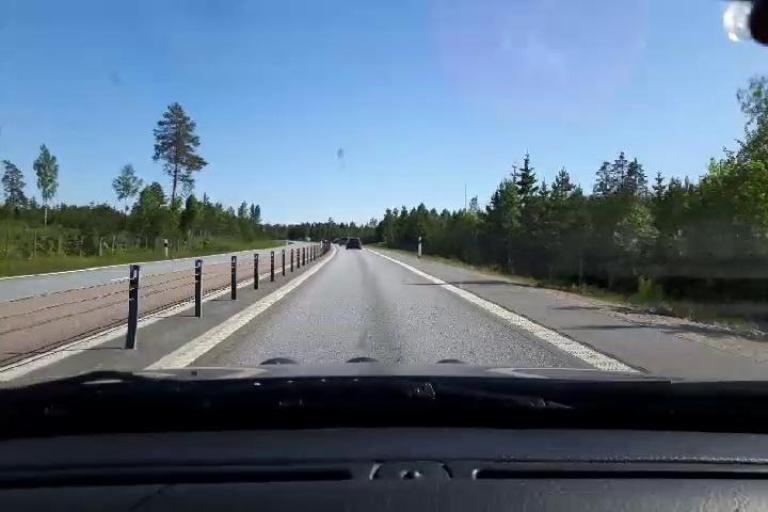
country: SE
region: Gaevleborg
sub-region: Gavle Kommun
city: Gavle
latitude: 60.7240
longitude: 17.0746
